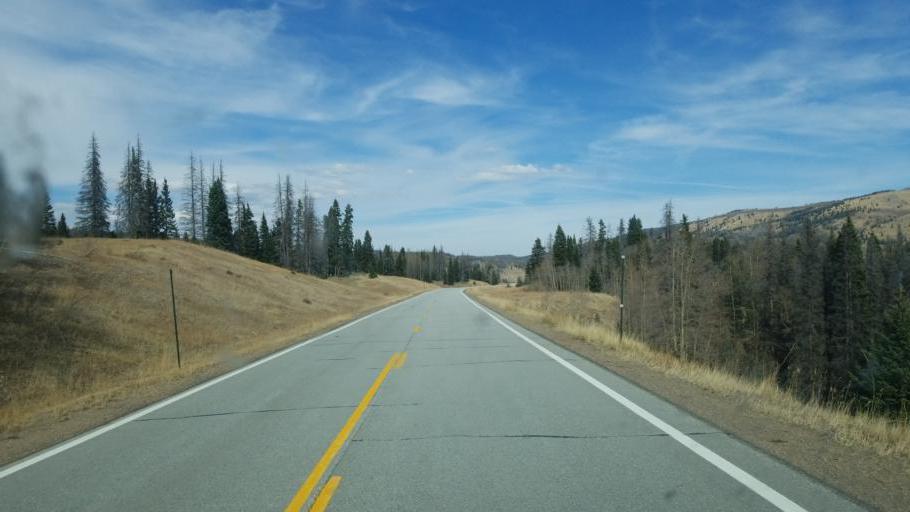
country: US
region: New Mexico
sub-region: Rio Arriba County
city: Chama
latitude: 37.0203
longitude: -106.4158
